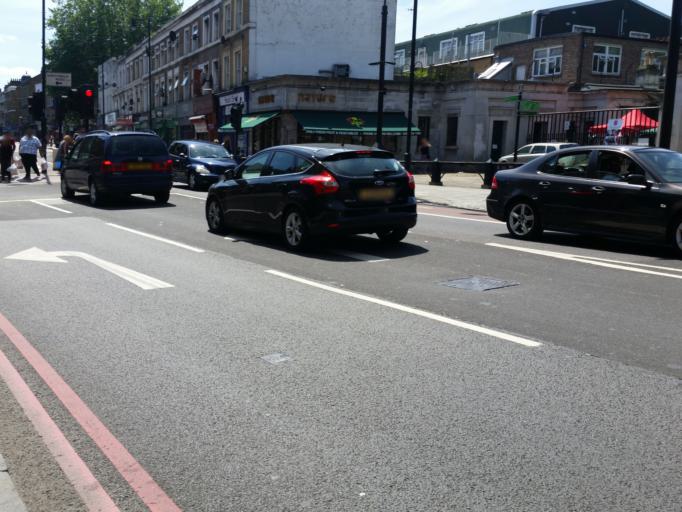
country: GB
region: England
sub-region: Greater London
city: Hackney
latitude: 51.5637
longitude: -0.0730
